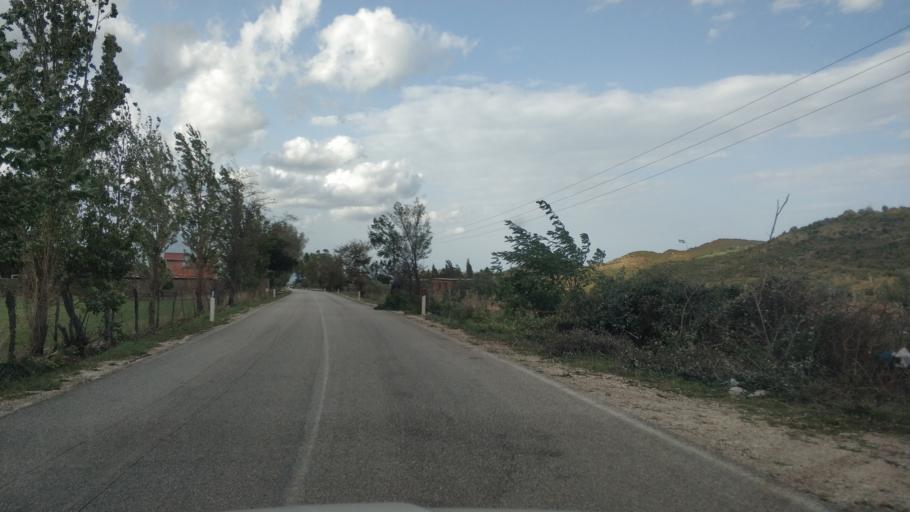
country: AL
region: Vlore
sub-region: Rrethi i Vlores
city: Orikum
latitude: 40.2804
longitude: 19.5023
